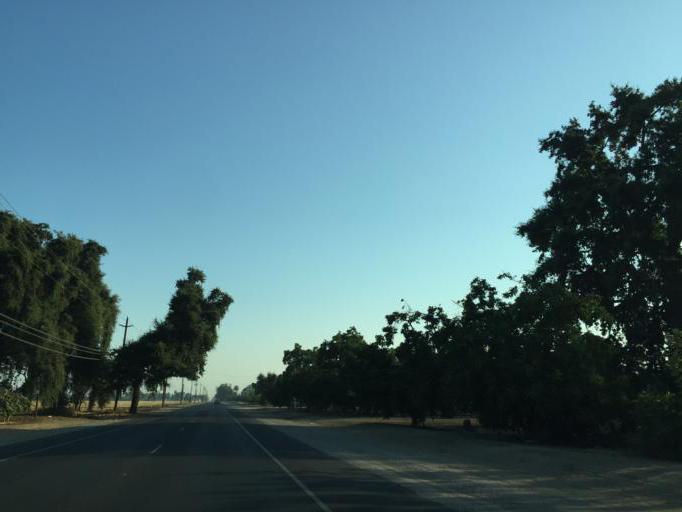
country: US
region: California
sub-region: Tulare County
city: Visalia
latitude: 36.3934
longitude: -119.2964
